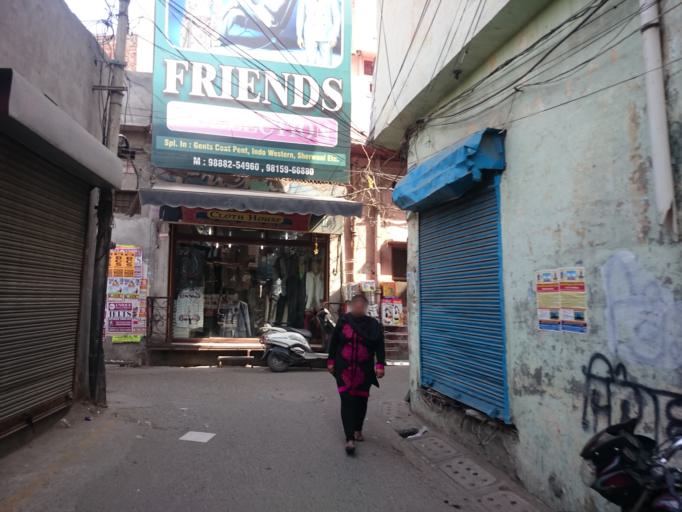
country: IN
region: Punjab
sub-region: Kapurthala
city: Phagwara
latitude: 31.2231
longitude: 75.7701
